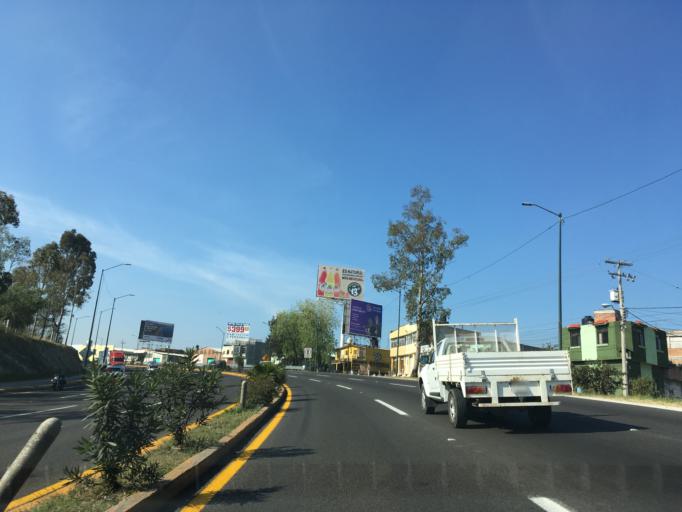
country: MX
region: Michoacan
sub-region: Tarimbaro
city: Fraccionamiento Privadas del Sol
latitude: 19.7372
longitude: -101.1815
